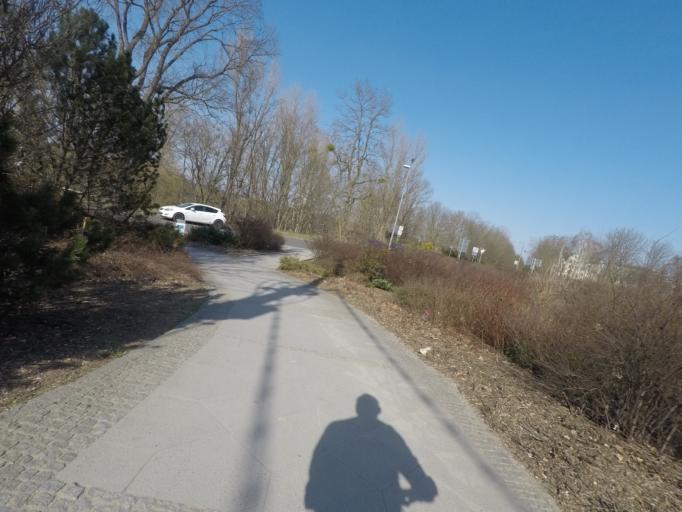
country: DE
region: Brandenburg
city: Eberswalde
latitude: 52.8344
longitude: 13.7995
